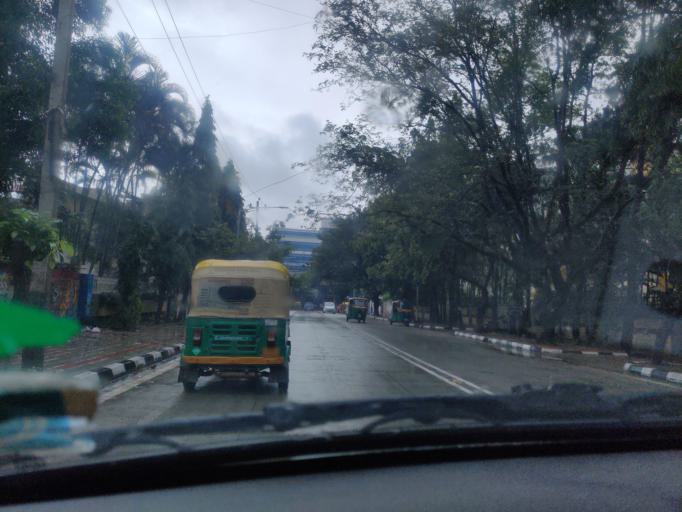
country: IN
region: Karnataka
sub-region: Bangalore Urban
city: Bangalore
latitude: 13.0243
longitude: 77.6325
